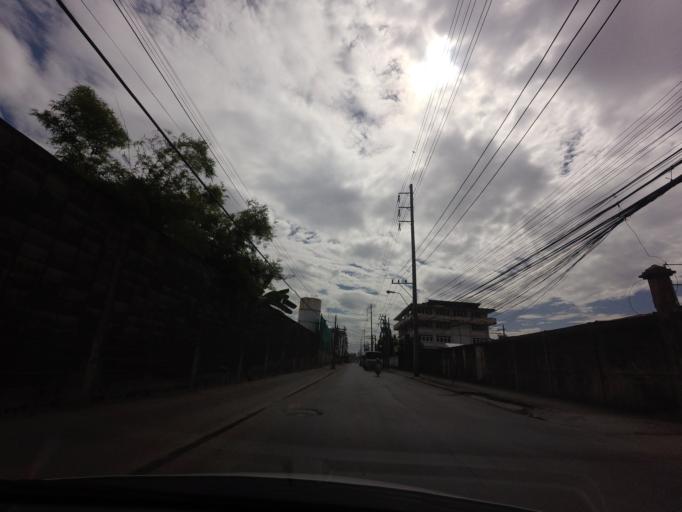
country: TH
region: Bangkok
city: Phra Khanong
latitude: 13.7010
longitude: 100.5892
